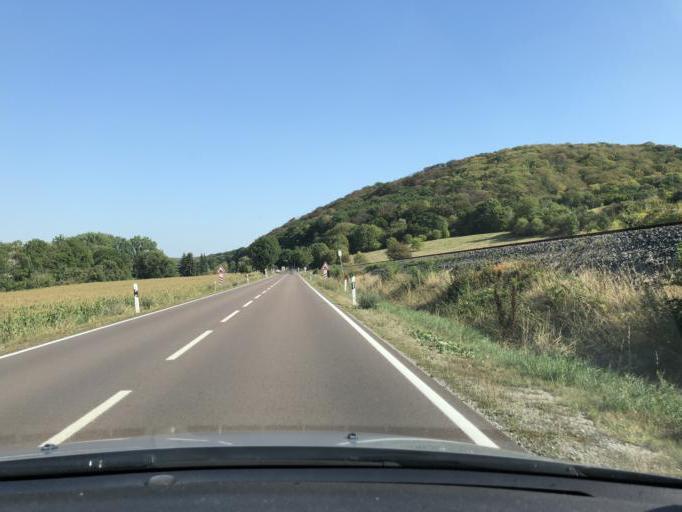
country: DE
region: Saxony-Anhalt
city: Laucha
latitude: 51.2163
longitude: 11.6990
